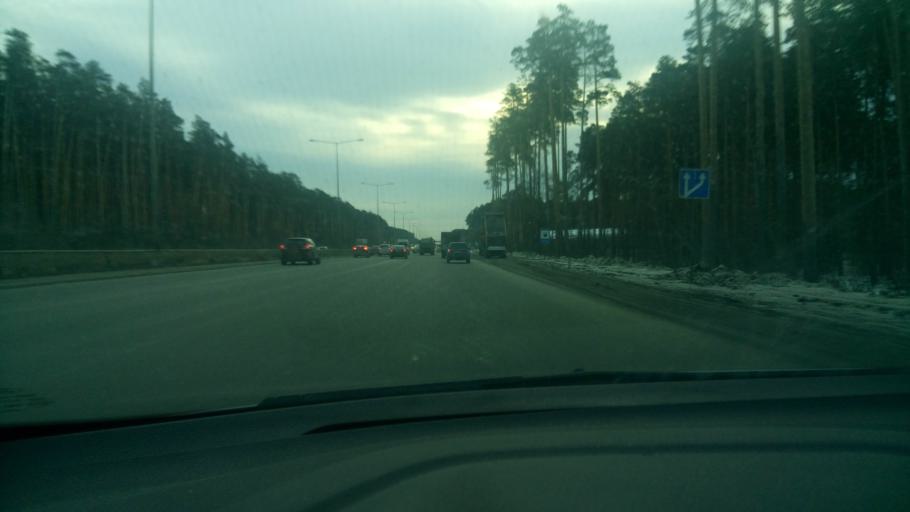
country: RU
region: Sverdlovsk
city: Yekaterinburg
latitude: 56.7918
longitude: 60.6646
